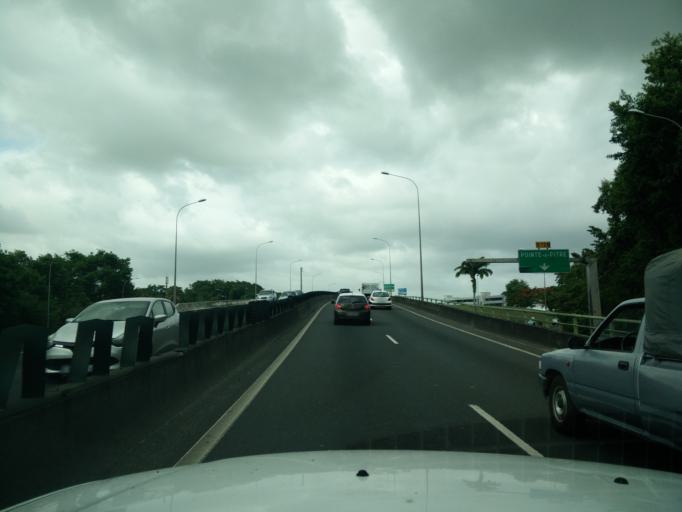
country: GP
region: Guadeloupe
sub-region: Guadeloupe
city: Pointe-a-Pitre
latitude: 16.2532
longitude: -61.5436
